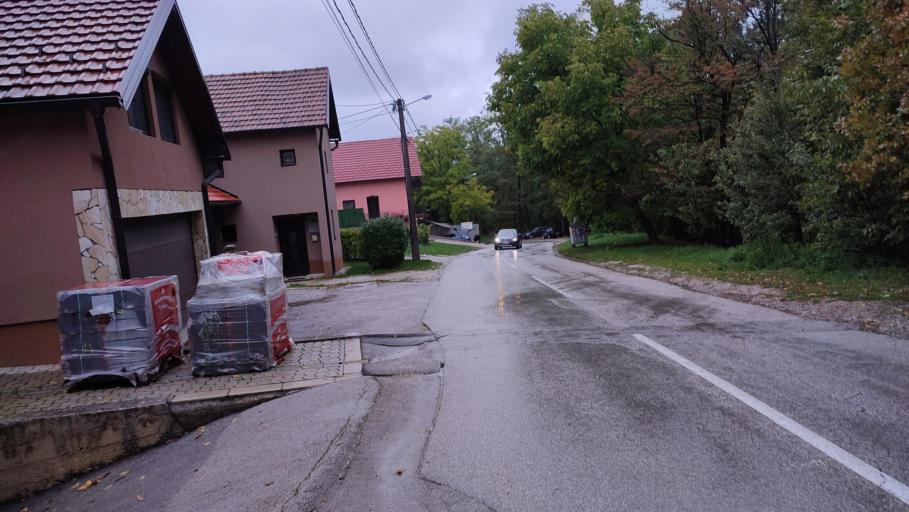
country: RS
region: Central Serbia
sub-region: Zlatiborski Okrug
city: Uzice
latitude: 43.8577
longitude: 19.8651
